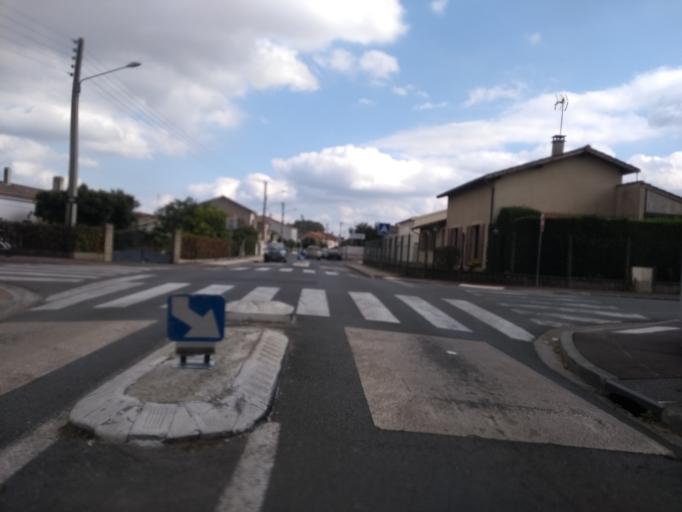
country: FR
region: Aquitaine
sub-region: Departement de la Gironde
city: Begles
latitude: 44.7968
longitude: -0.5657
